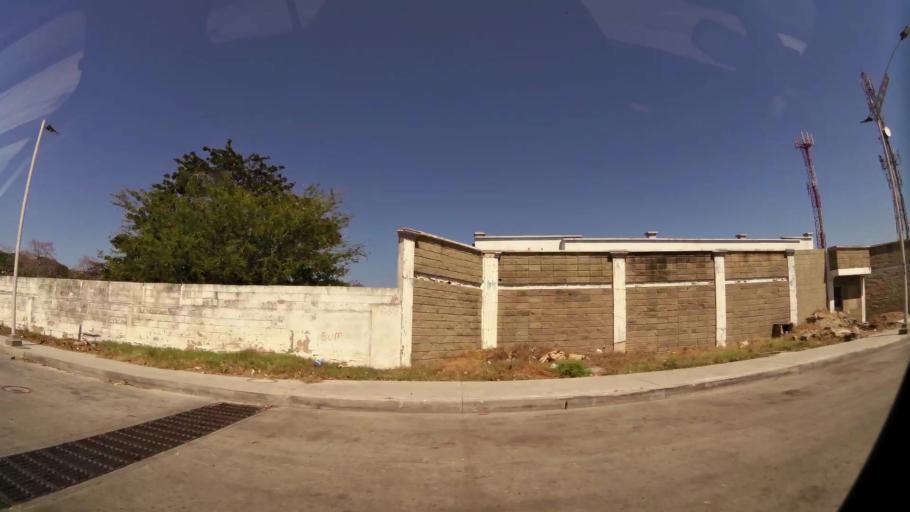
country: CO
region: Atlantico
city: Barranquilla
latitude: 10.9729
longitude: -74.7658
